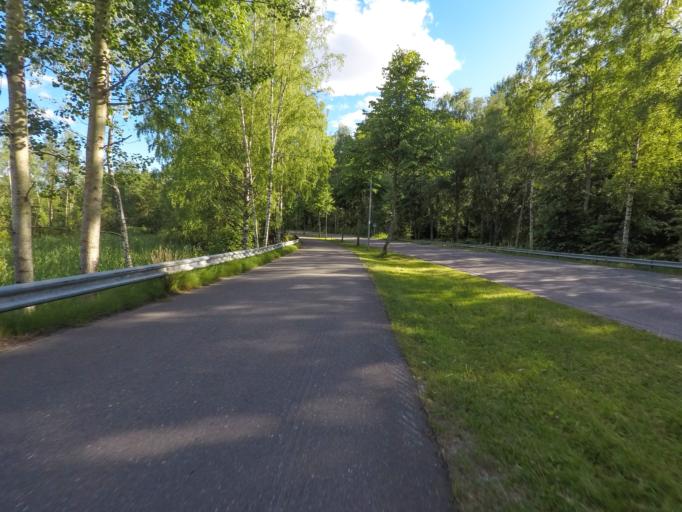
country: FI
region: South Karelia
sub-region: Lappeenranta
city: Lappeenranta
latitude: 61.0740
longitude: 28.1505
